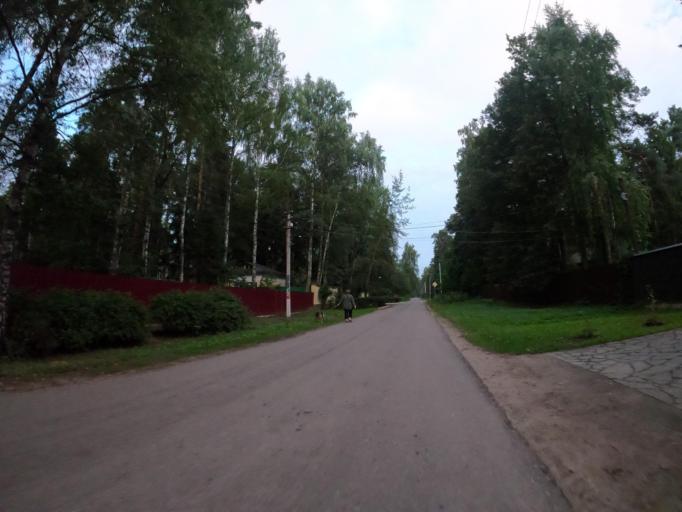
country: RU
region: Moskovskaya
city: Il'inskiy
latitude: 55.6273
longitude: 38.1012
